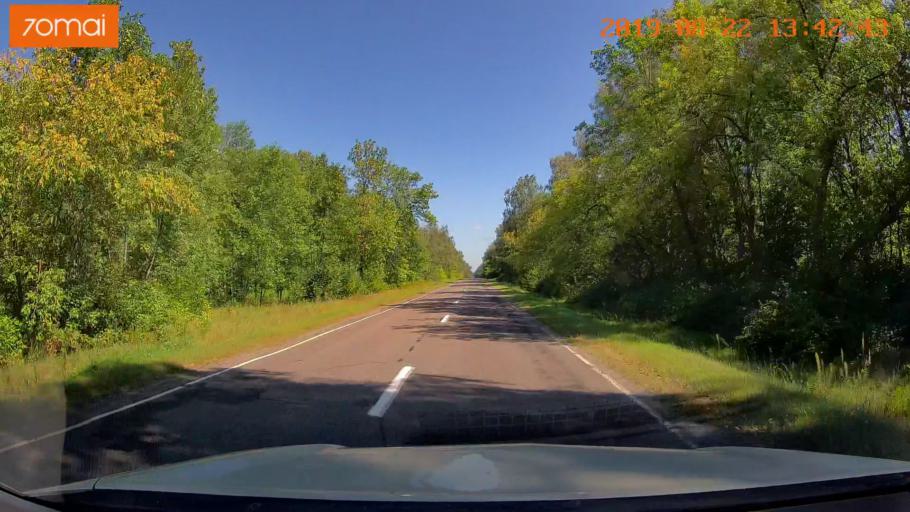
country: BY
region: Mogilev
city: Asipovichy
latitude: 53.2414
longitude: 28.4190
